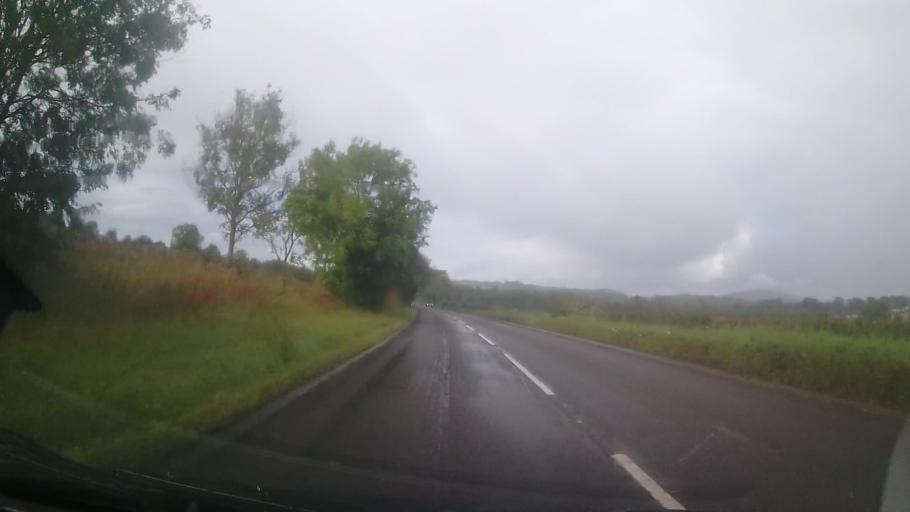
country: GB
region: England
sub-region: Shropshire
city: Much Wenlock
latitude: 52.5881
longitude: -2.5519
